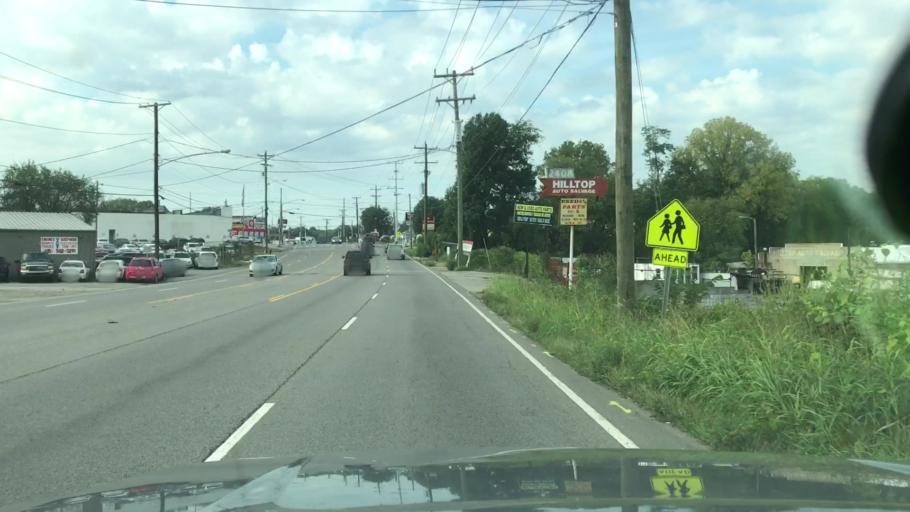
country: US
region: Tennessee
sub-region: Davidson County
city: Nashville
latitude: 36.2095
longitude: -86.7665
